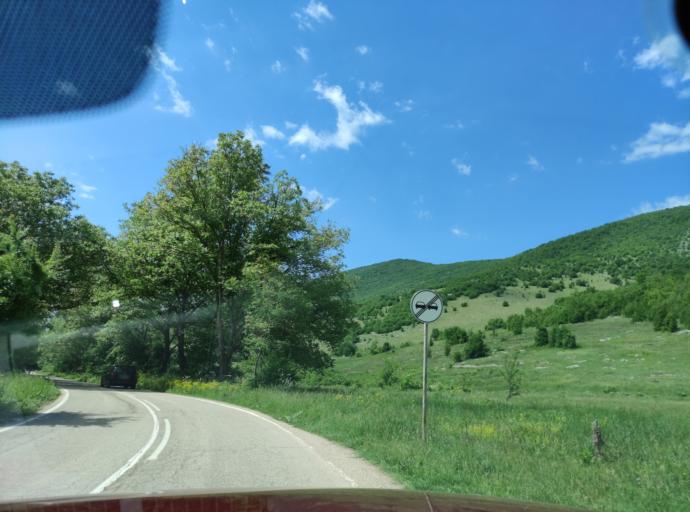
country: BG
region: Montana
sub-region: Obshtina Chiprovtsi
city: Chiprovtsi
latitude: 43.4876
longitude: 22.8144
